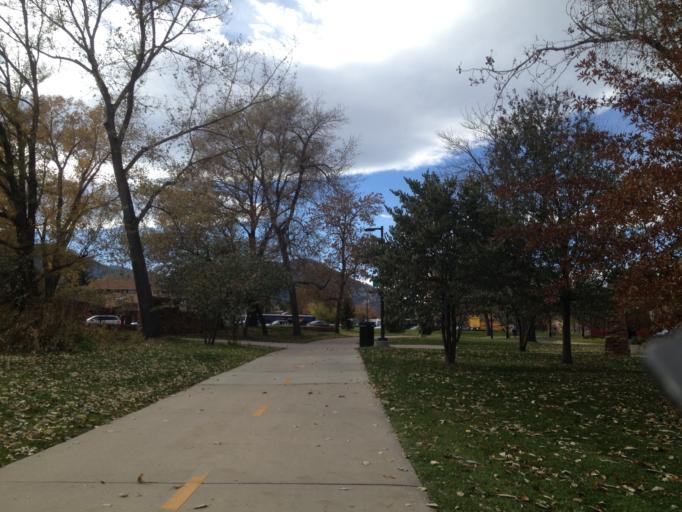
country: US
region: Colorado
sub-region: Boulder County
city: Boulder
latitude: 40.0005
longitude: -105.2629
